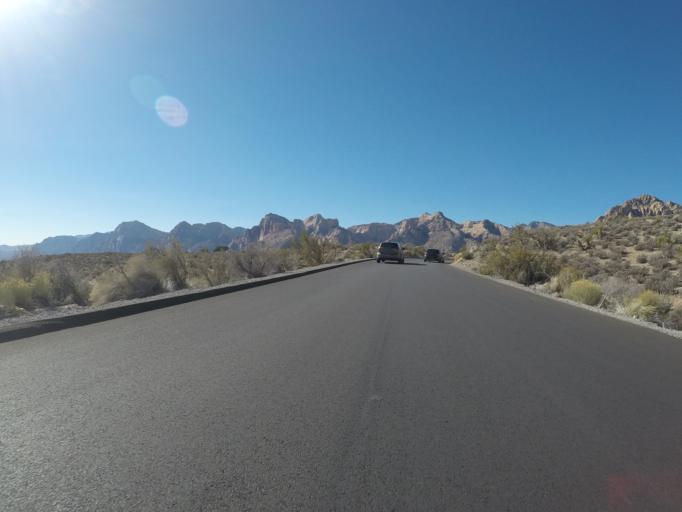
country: US
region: Nevada
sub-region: Clark County
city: Summerlin South
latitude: 36.1720
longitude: -115.4642
